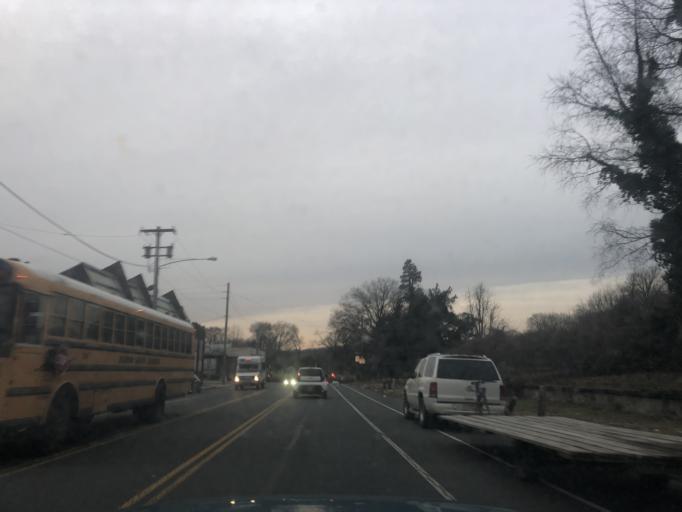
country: US
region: Pennsylvania
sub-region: Montgomery County
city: Bala-Cynwyd
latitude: 39.9980
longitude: -75.1856
